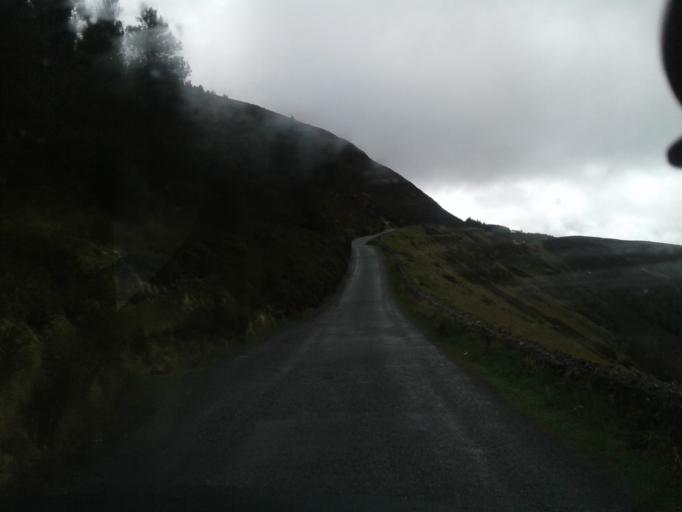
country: IE
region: Leinster
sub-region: Wicklow
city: Enniskerry
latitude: 53.1125
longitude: -6.2604
